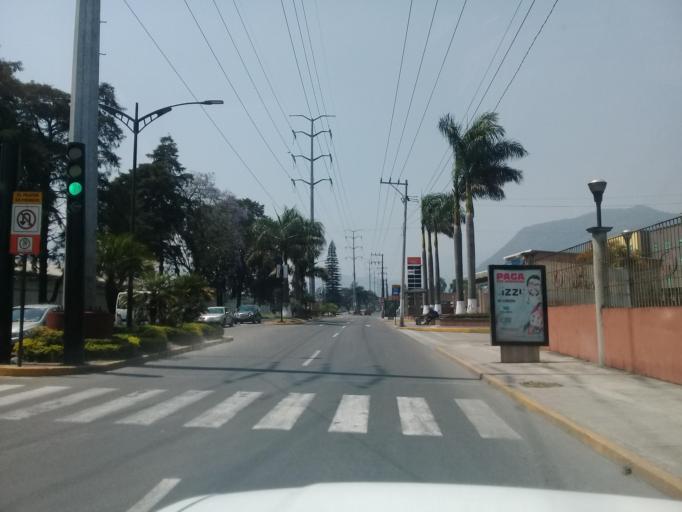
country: MX
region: Veracruz
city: Ixtac Zoquitlan
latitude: 18.8616
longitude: -97.0570
